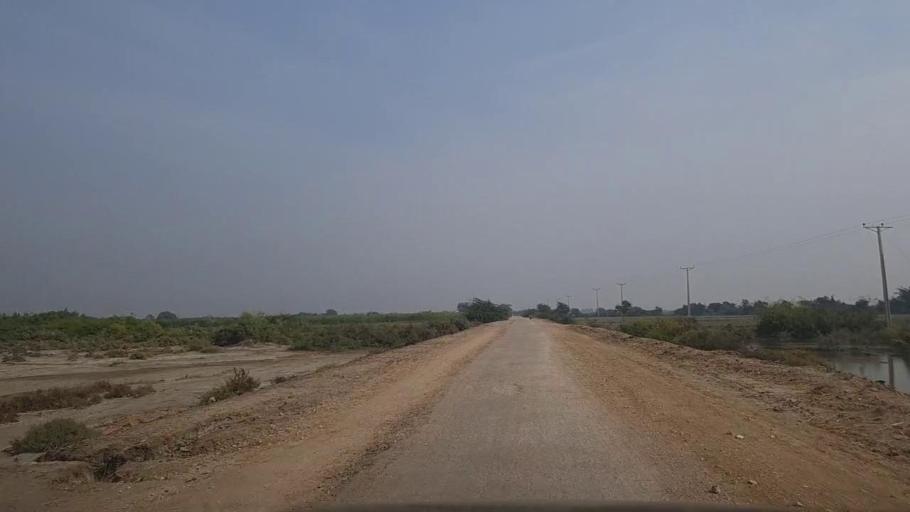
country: PK
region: Sindh
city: Mirpur Sakro
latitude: 24.4026
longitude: 67.7435
